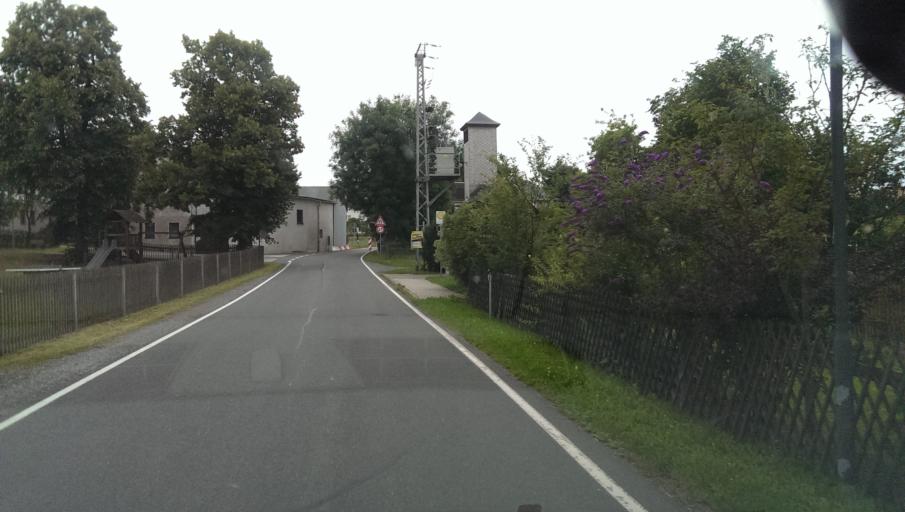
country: DE
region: Thuringia
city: Dittersdorf
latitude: 50.6459
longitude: 11.8343
